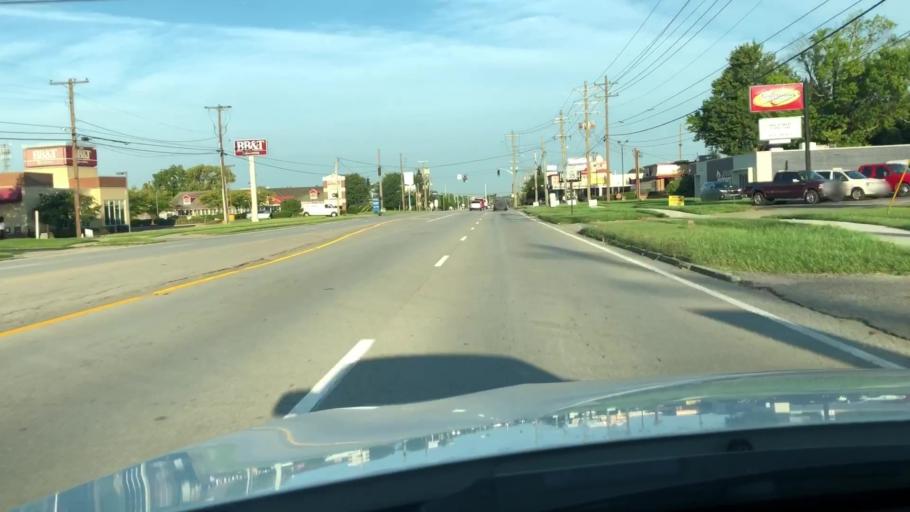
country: US
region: Kentucky
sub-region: Jefferson County
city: Saint Regis Park
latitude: 38.2196
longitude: -85.6208
